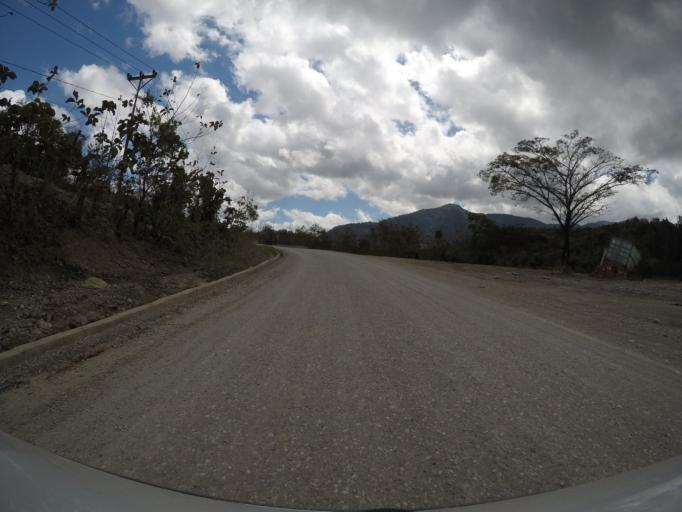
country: TL
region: Viqueque
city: Viqueque
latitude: -8.8100
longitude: 126.3810
